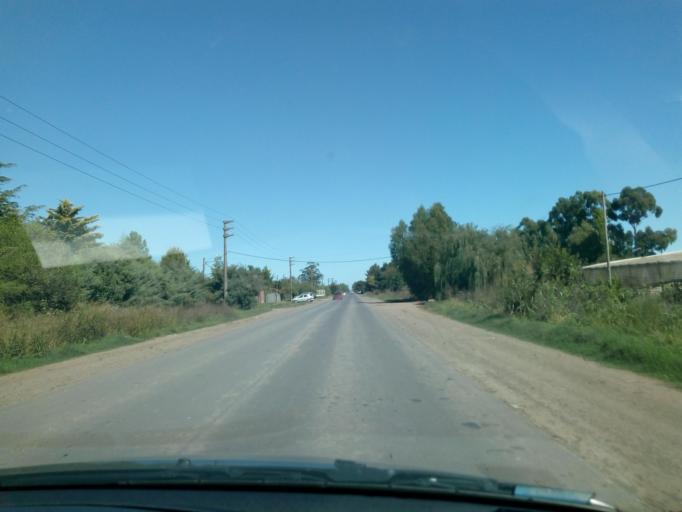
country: AR
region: Buenos Aires
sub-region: Partido de La Plata
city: La Plata
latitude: -35.0078
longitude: -58.0247
